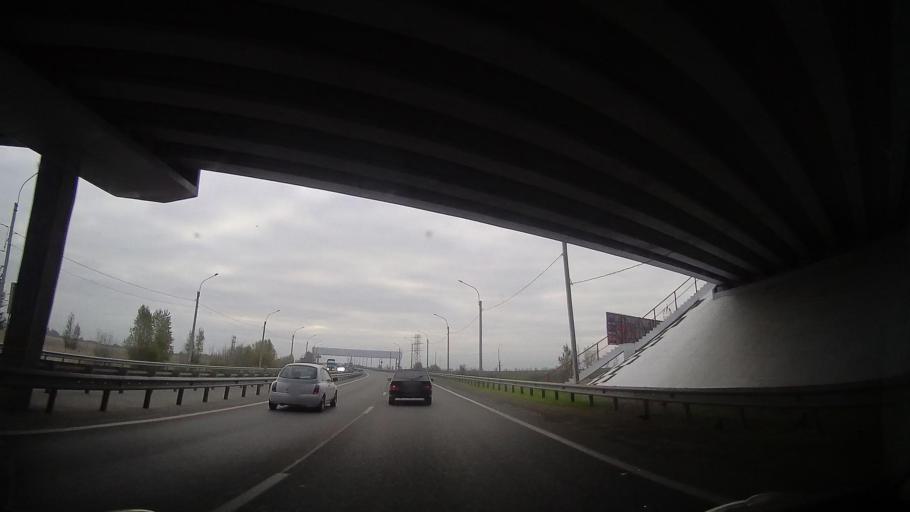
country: RU
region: Rostov
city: Bataysk
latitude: 47.1695
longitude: 39.7473
